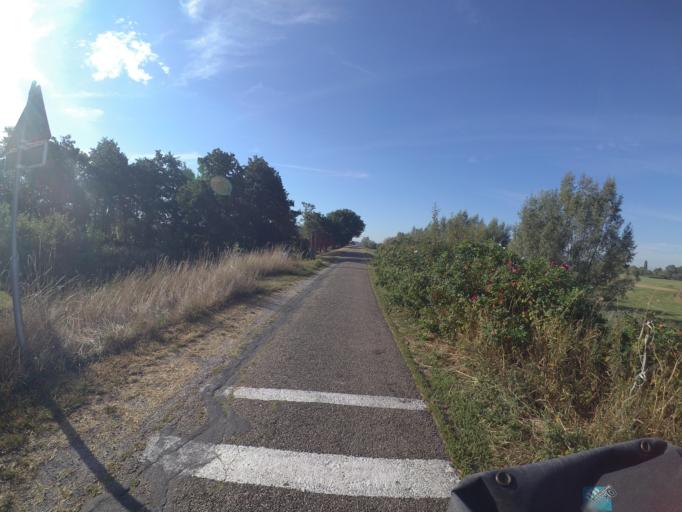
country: NL
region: Overijssel
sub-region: Gemeente Zwartewaterland
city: Hasselt
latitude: 52.5685
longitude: 6.1101
